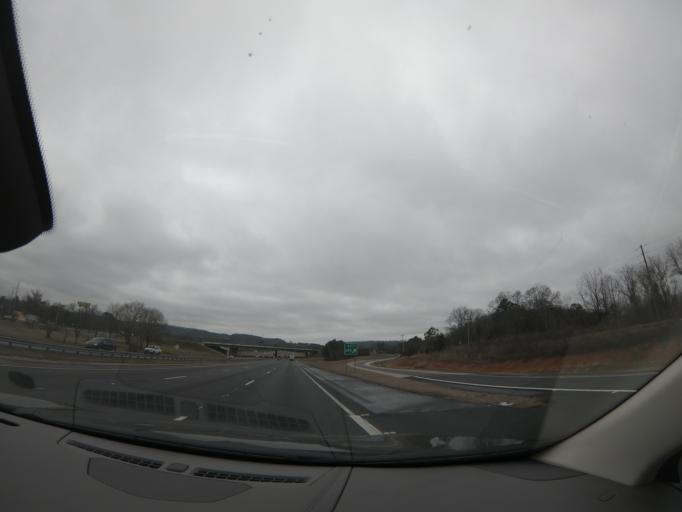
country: US
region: Georgia
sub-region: Catoosa County
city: Ringgold
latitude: 34.8913
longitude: -85.0717
